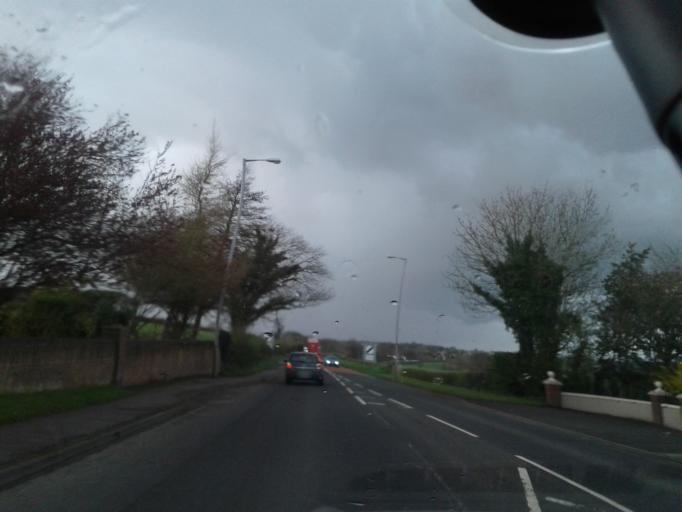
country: GB
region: Northern Ireland
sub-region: Strabane District
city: Sion Mills
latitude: 54.7919
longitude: -7.4743
